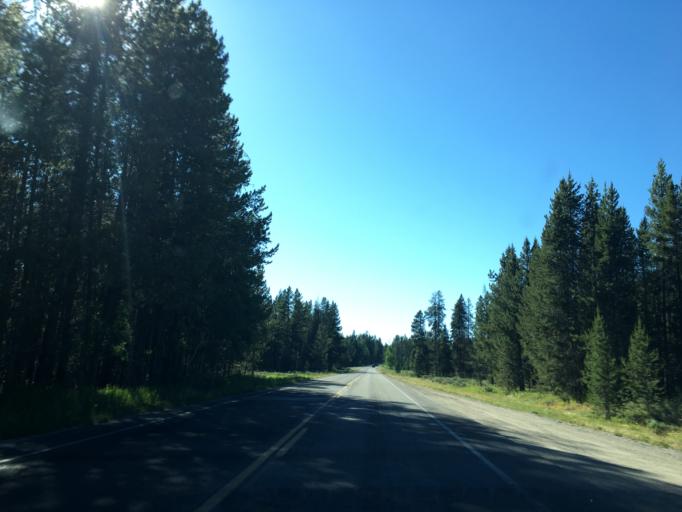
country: US
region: Wyoming
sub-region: Teton County
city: Jackson
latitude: 43.8543
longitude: -110.5205
